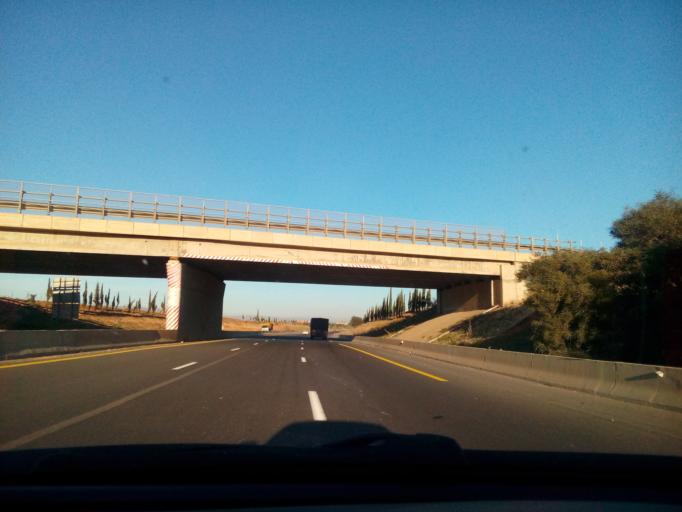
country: DZ
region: Relizane
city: Djidiouia
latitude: 35.8966
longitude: 0.7107
